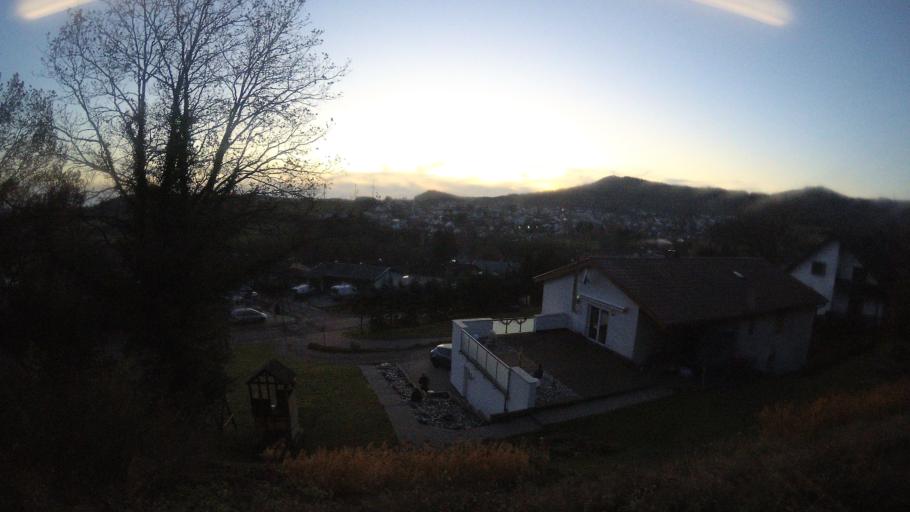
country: DE
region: Rheinland-Pfalz
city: Reichweiler
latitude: 49.5255
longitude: 7.2715
